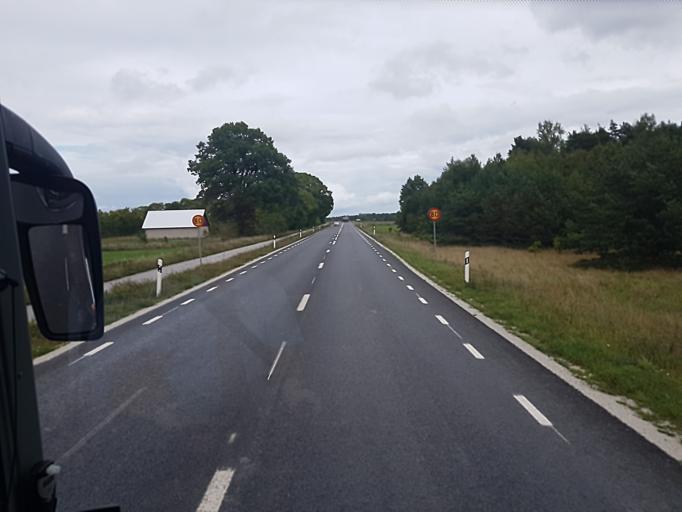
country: SE
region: Gotland
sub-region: Gotland
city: Vibble
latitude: 57.5909
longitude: 18.2423
